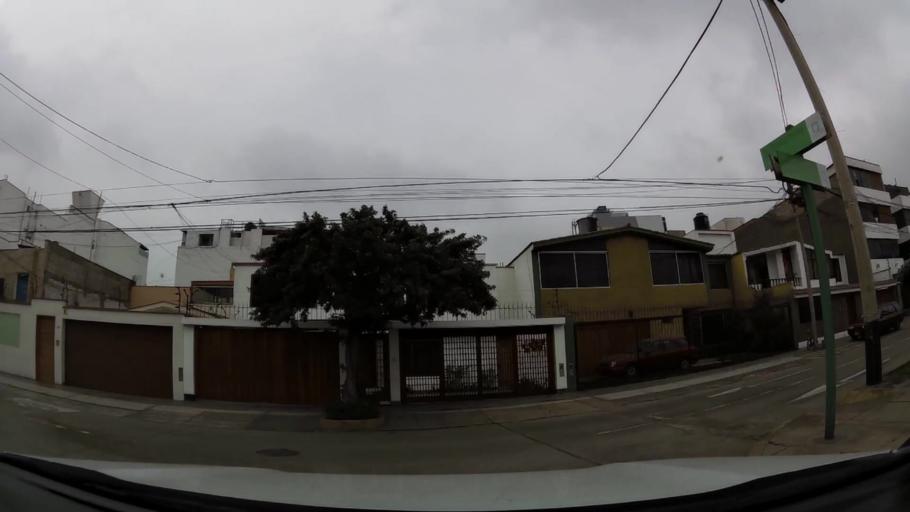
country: PE
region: Lima
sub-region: Lima
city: Surco
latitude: -12.1284
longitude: -77.0090
